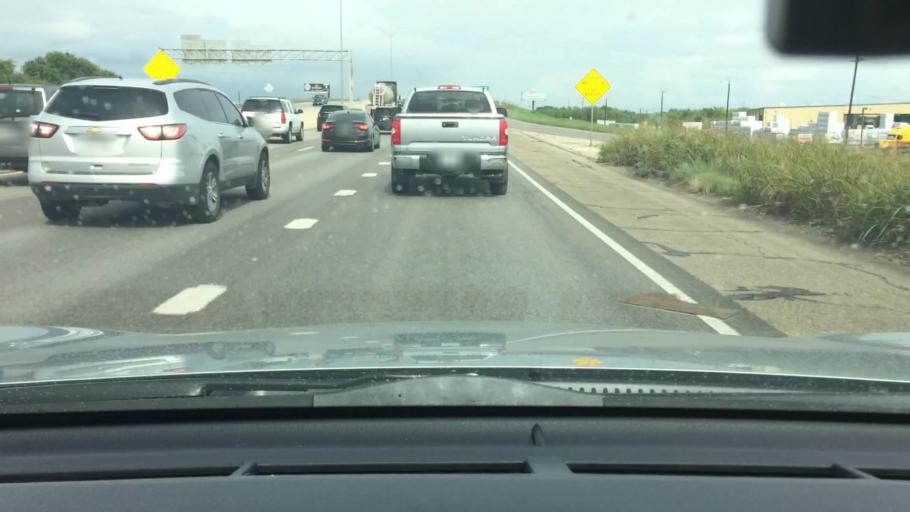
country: US
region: Texas
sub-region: Bexar County
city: Kirby
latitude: 29.4315
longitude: -98.4039
